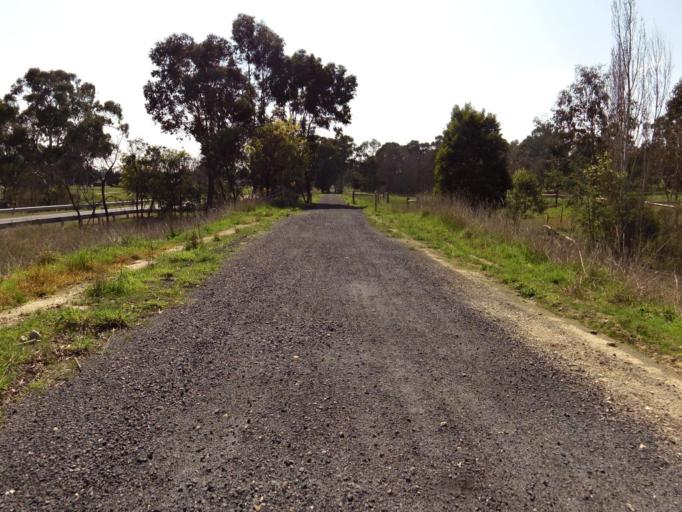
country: AU
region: Victoria
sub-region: Murrindindi
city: Alexandra
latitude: -37.1296
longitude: 145.5953
